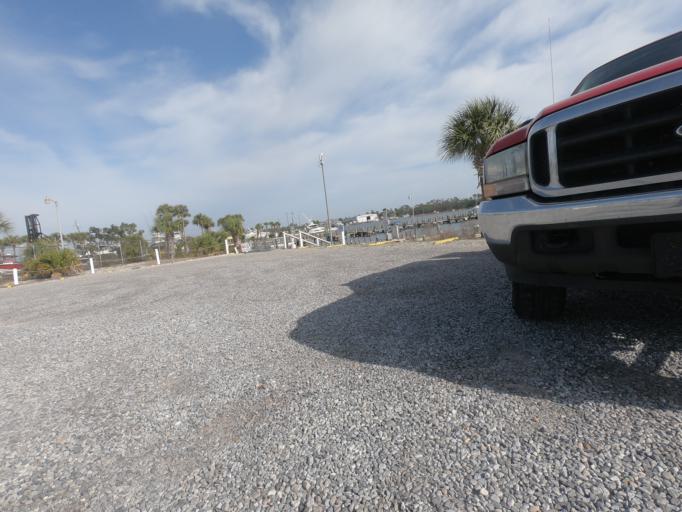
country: US
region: Florida
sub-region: Bay County
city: Lower Grand Lagoon
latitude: 30.1428
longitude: -85.7464
